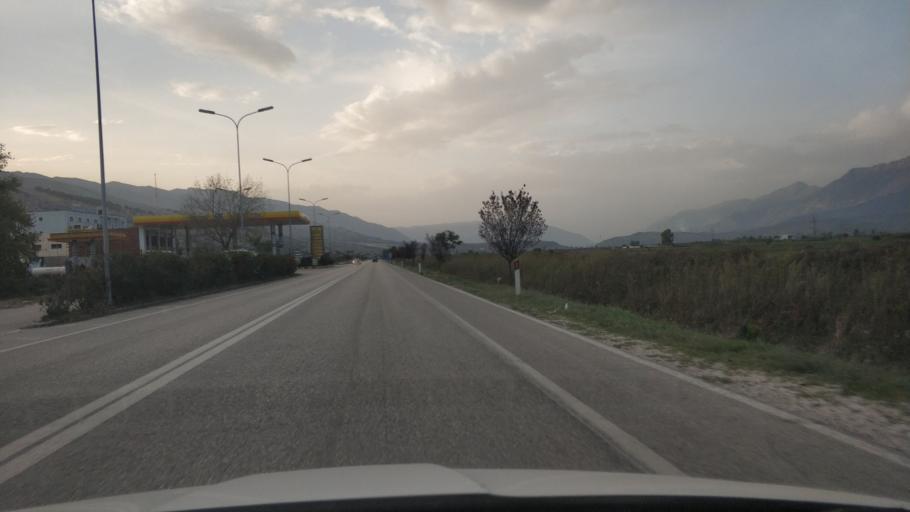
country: AL
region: Gjirokaster
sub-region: Rrethi i Gjirokastres
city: Dervician
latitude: 40.0068
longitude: 20.2078
